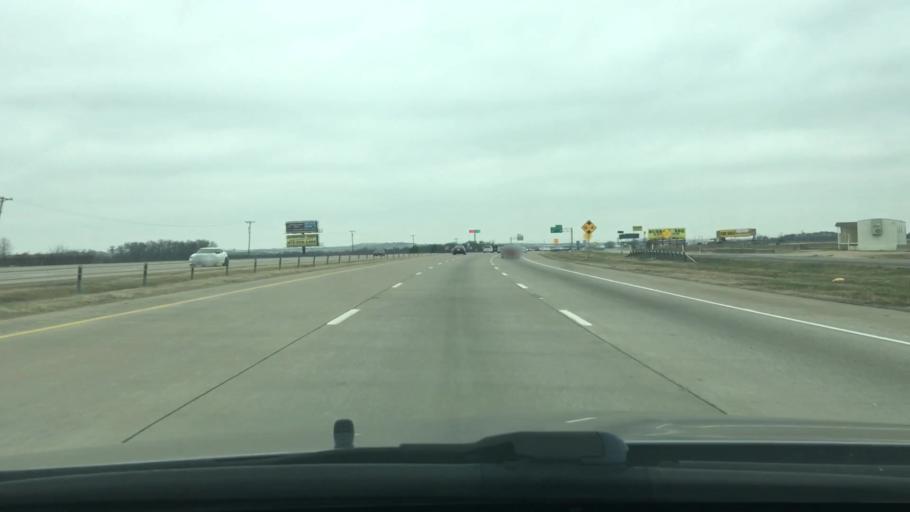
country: US
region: Texas
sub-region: Ellis County
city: Palmer
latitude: 32.4253
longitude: -96.6585
